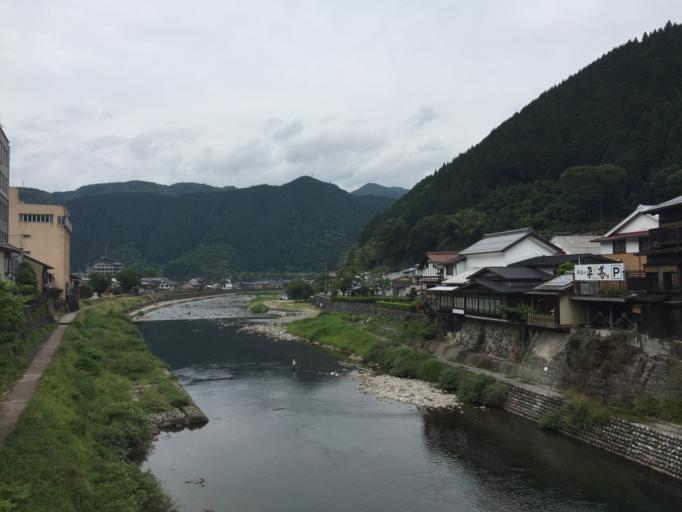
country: JP
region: Gifu
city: Gujo
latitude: 35.7495
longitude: 136.9574
